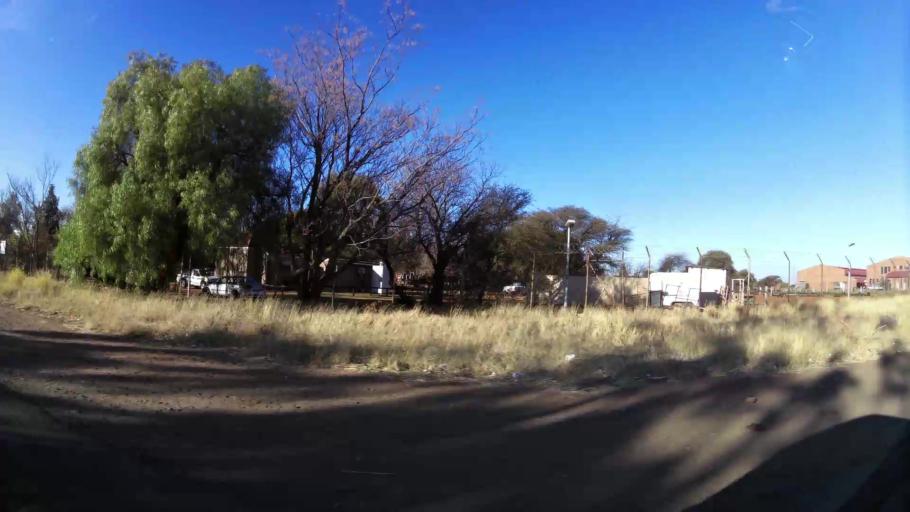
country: ZA
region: Northern Cape
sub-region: Frances Baard District Municipality
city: Kimberley
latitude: -28.7432
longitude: 24.7267
